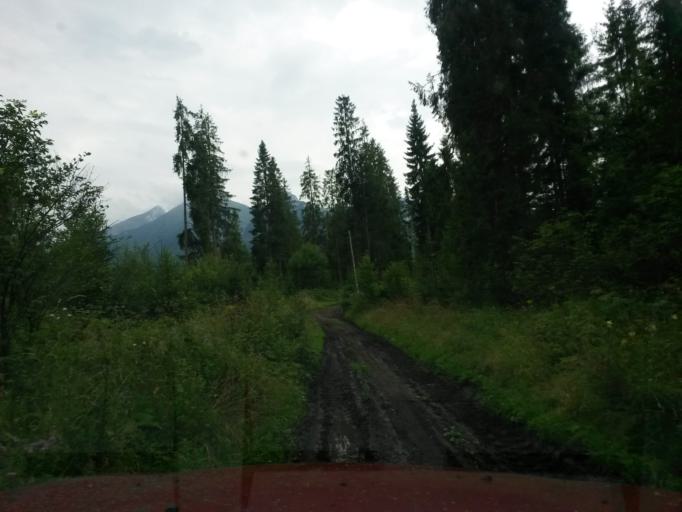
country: PL
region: Lesser Poland Voivodeship
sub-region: Powiat tatrzanski
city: Bukowina Tatrzanska
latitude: 49.2926
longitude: 20.1718
